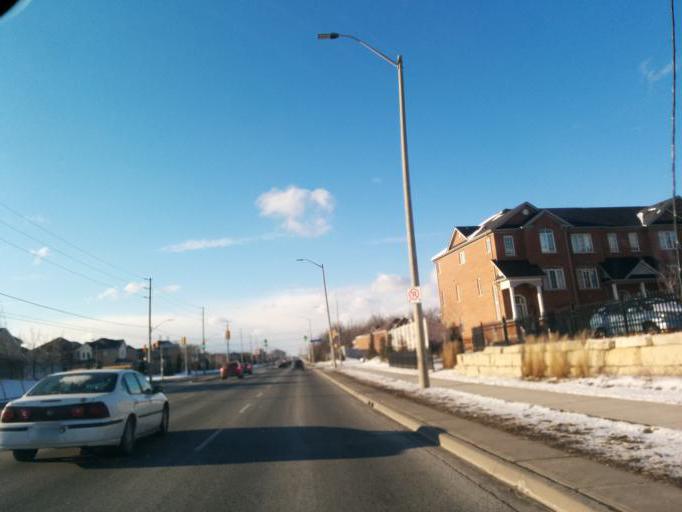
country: CA
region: Ontario
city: Brampton
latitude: 43.6380
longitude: -79.7187
